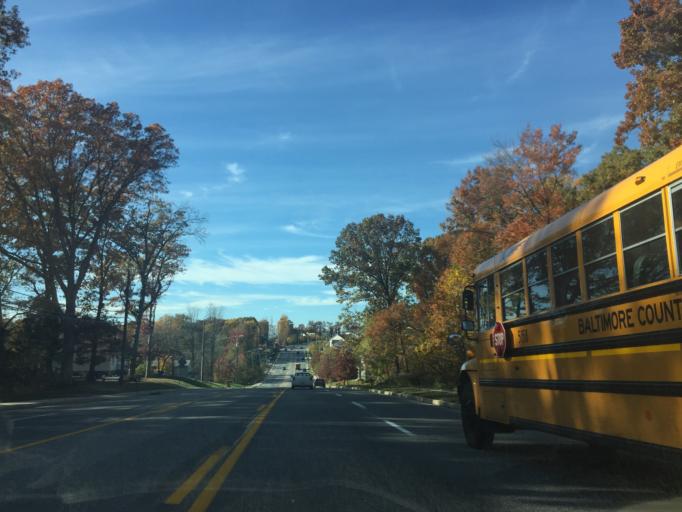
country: US
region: Maryland
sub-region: Baltimore County
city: Rossville
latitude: 39.3582
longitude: -76.4934
